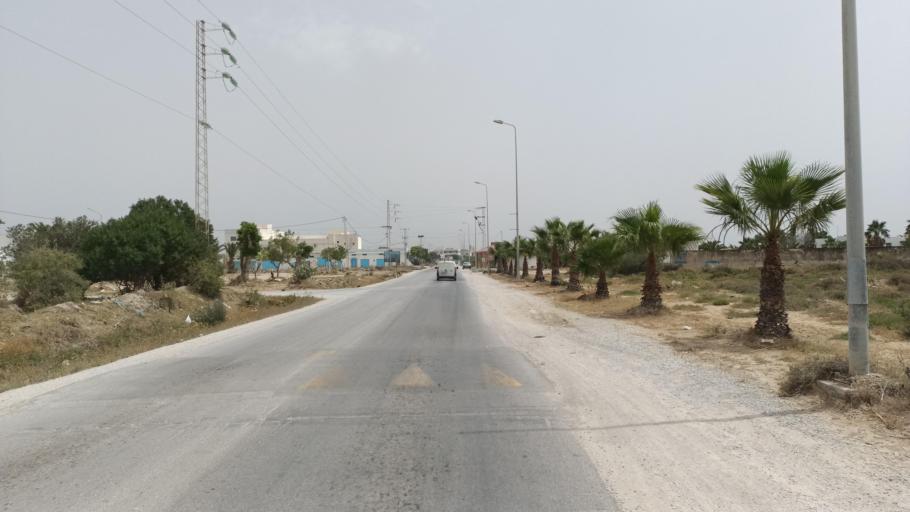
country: TN
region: Nabul
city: Manzil Bu Zalafah
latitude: 36.7114
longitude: 10.4818
